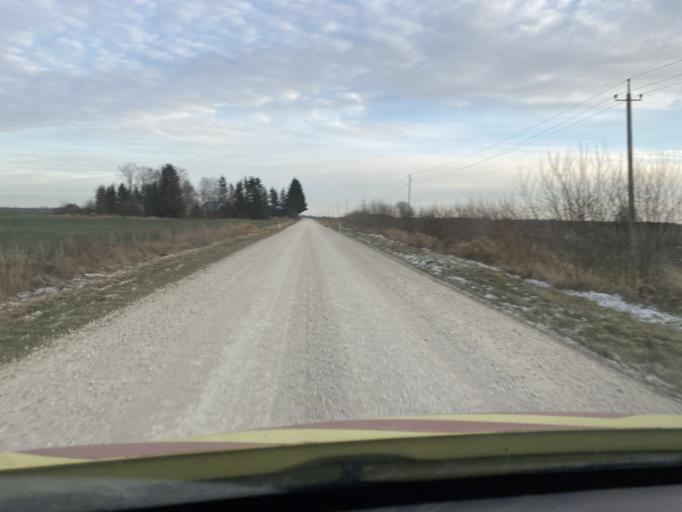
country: EE
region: Jogevamaa
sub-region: Poltsamaa linn
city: Poltsamaa
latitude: 58.5825
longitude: 26.0620
